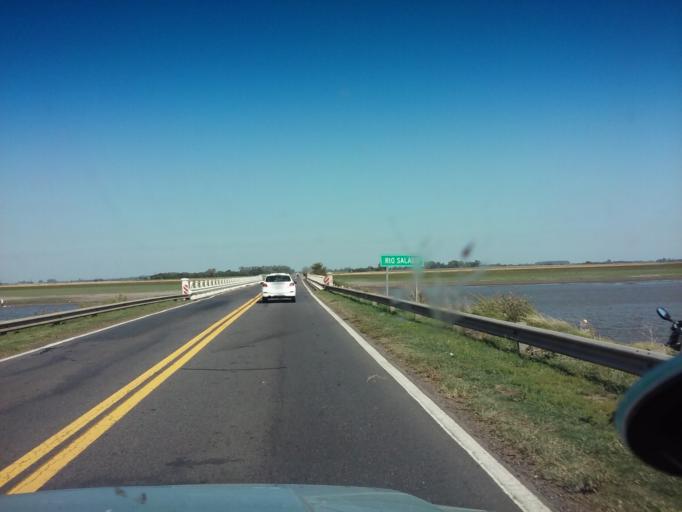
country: AR
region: Buenos Aires
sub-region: Partido de Alberti
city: Alberti
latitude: -35.0626
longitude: -60.2922
